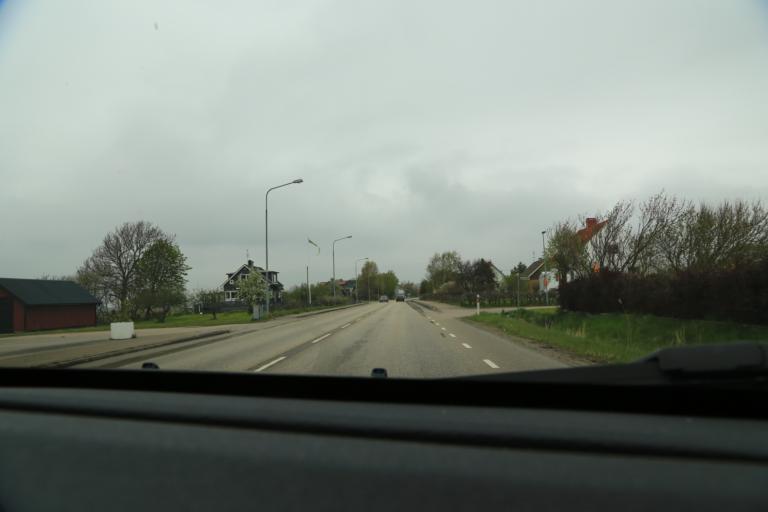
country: SE
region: Halland
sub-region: Varbergs Kommun
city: Veddige
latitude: 57.2164
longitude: 12.2221
